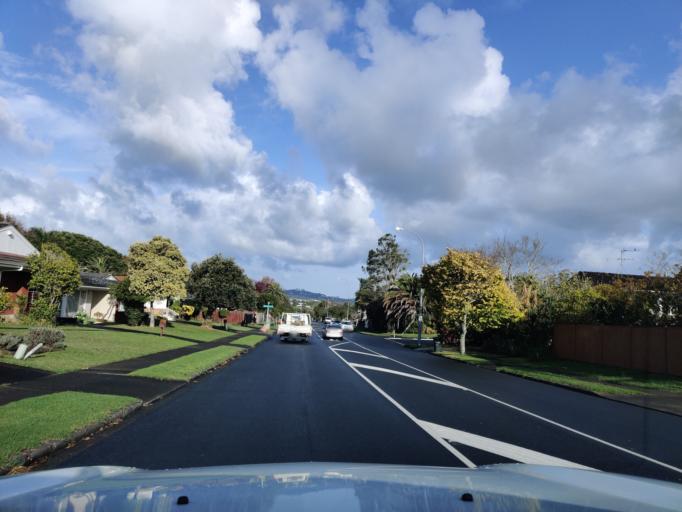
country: NZ
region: Auckland
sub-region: Auckland
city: Pakuranga
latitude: -36.9056
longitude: 174.8960
